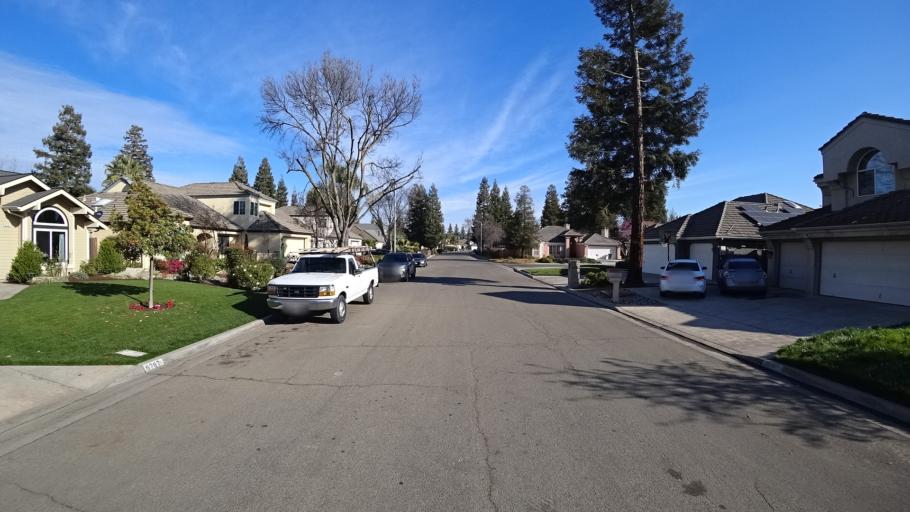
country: US
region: California
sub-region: Fresno County
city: West Park
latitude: 36.8275
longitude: -119.8619
